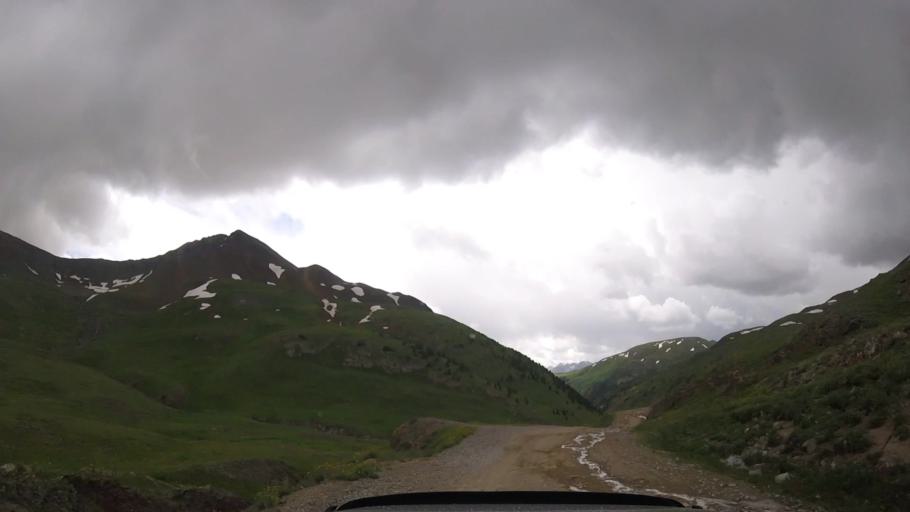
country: US
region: Colorado
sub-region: Ouray County
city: Ouray
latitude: 37.9521
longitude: -107.5744
